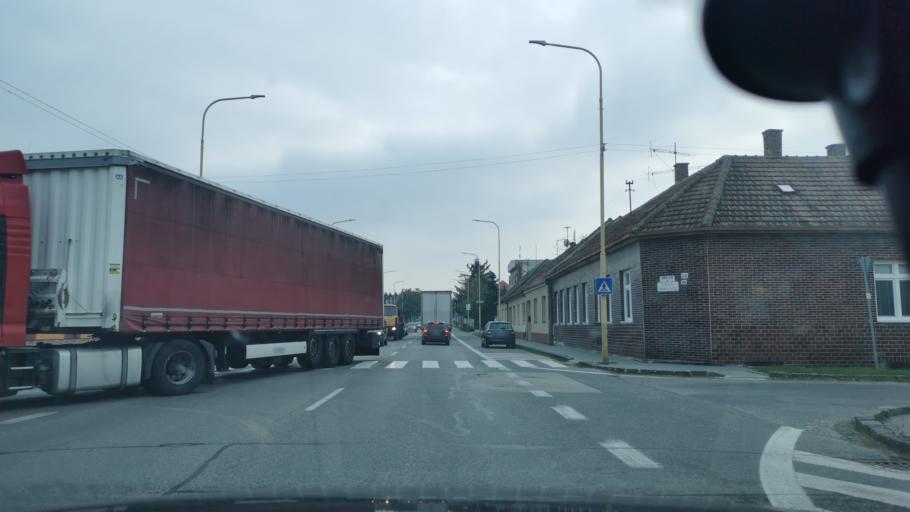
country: SK
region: Trnavsky
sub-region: Okres Skalica
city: Holic
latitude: 48.8161
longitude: 17.1624
